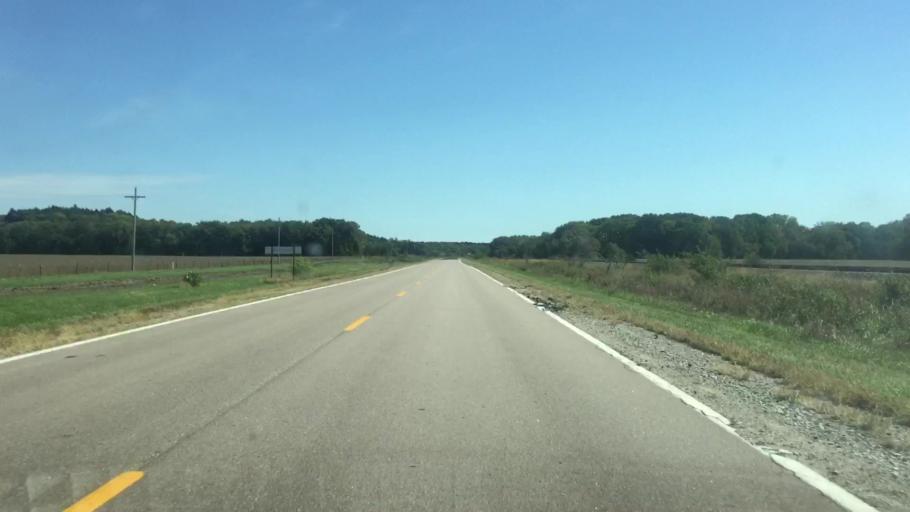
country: US
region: Nebraska
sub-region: Jefferson County
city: Fairbury
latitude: 40.0770
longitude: -97.0847
